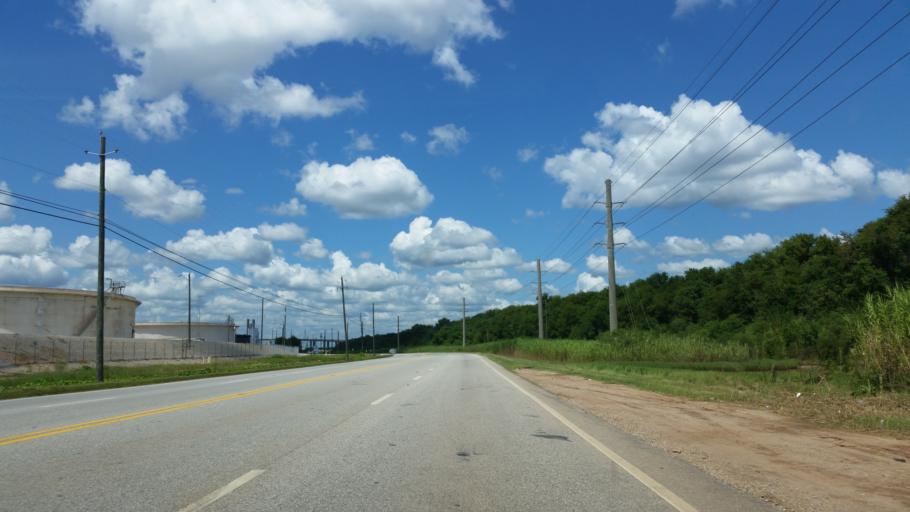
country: US
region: Alabama
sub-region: Mobile County
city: Mobile
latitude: 30.7131
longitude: -88.0335
